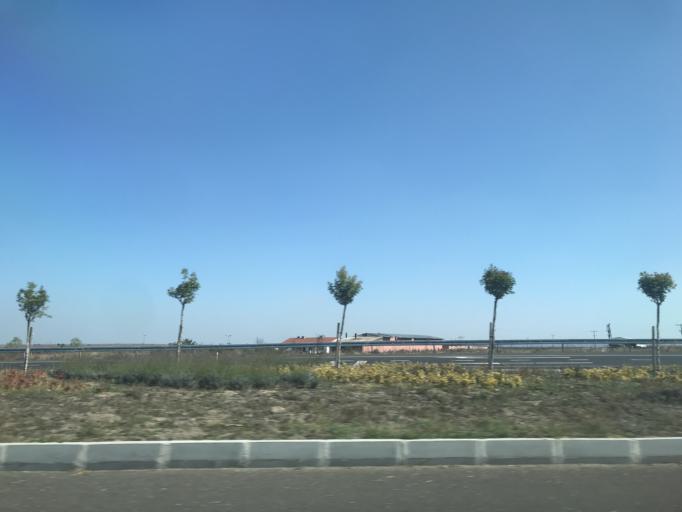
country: TR
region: Tekirdag
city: Muratli
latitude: 41.1748
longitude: 27.5382
